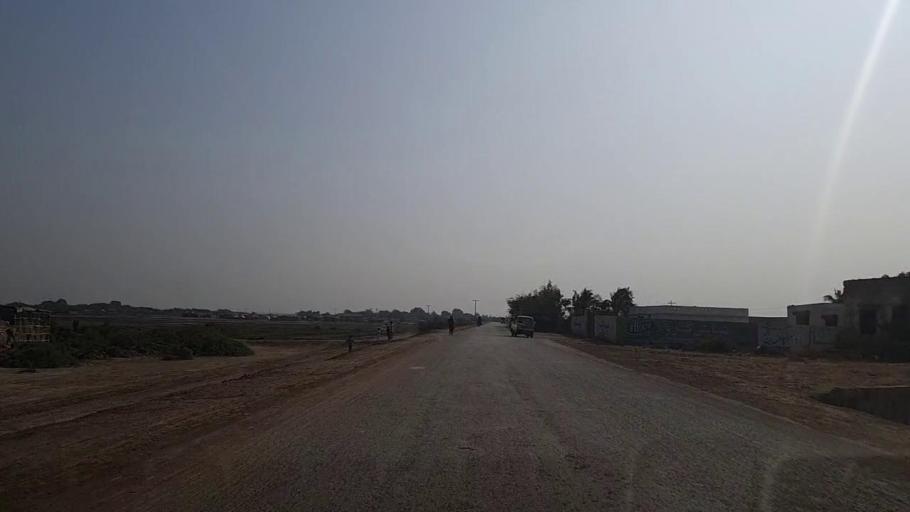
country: PK
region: Sindh
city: Keti Bandar
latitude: 24.2358
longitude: 67.6079
